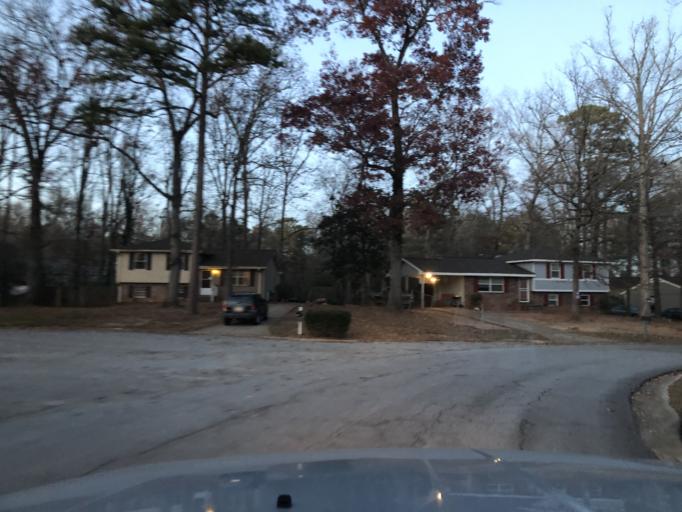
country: US
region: Georgia
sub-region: Clayton County
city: Jonesboro
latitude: 33.5250
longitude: -84.3924
